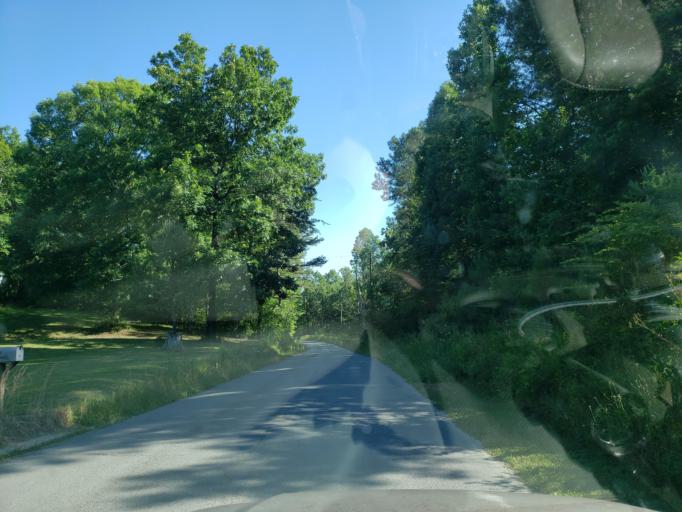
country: US
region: Georgia
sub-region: Whitfield County
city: Dalton
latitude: 34.6701
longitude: -85.1095
